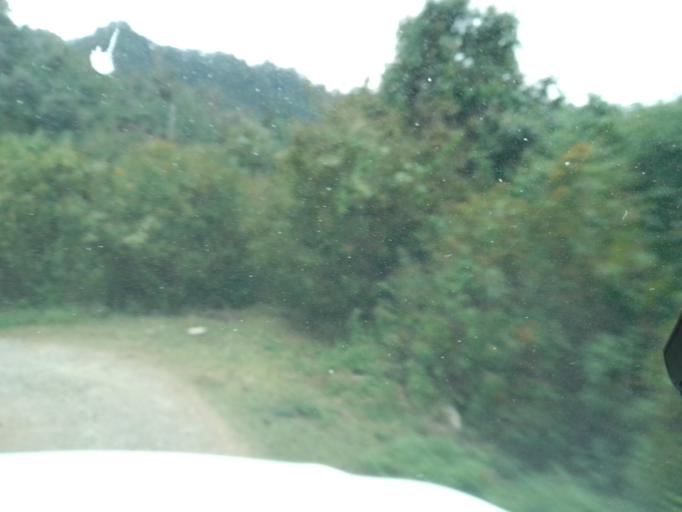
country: MX
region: Chiapas
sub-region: Cacahoatan
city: Benito Juarez
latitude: 15.2088
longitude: -92.2237
